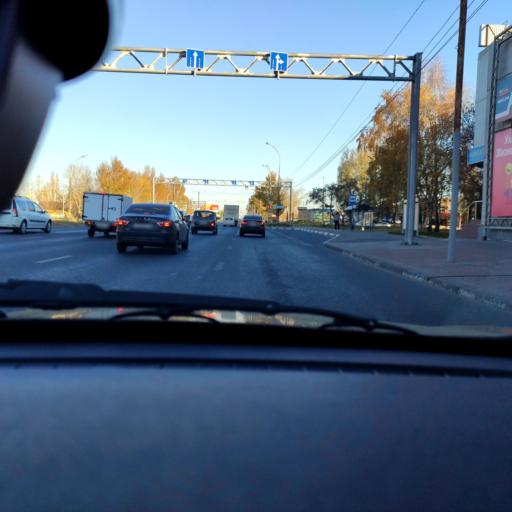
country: RU
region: Samara
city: Tol'yatti
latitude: 53.5363
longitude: 49.2837
